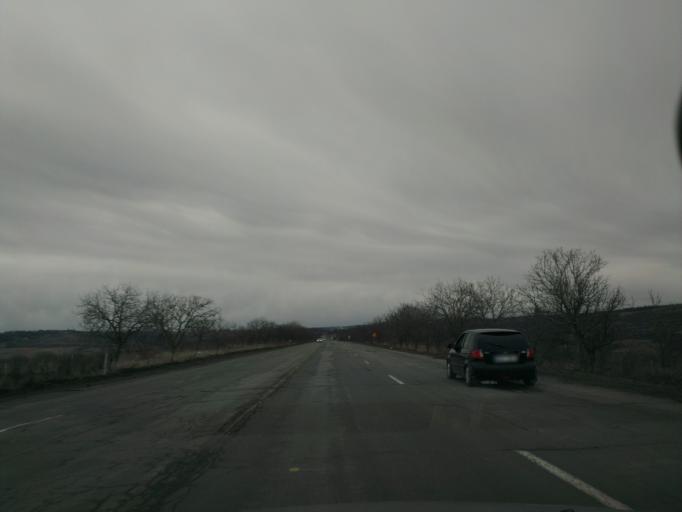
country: MD
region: Laloveni
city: Ialoveni
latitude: 46.9966
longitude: 28.7353
